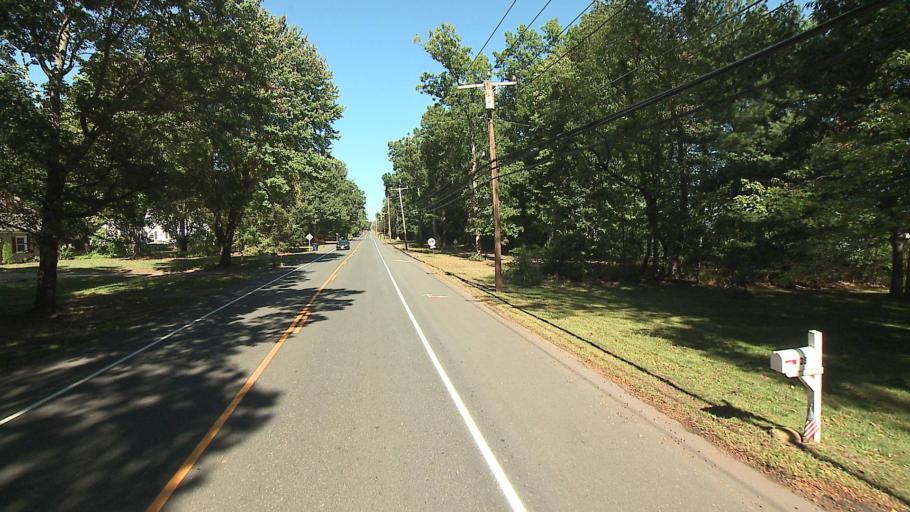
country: US
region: Connecticut
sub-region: Hartford County
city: Salmon Brook
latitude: 41.9233
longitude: -72.7913
